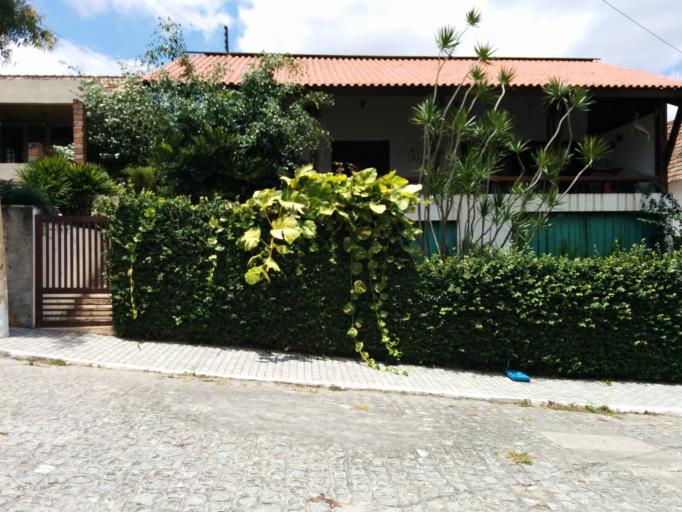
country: BR
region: Pernambuco
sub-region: Gravata
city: Gravata
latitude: -8.1935
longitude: -35.5619
